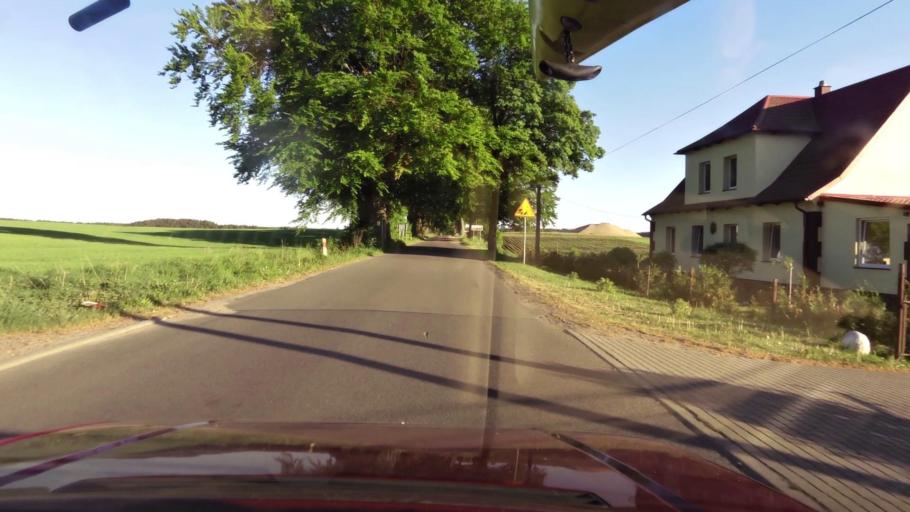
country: PL
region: West Pomeranian Voivodeship
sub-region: Powiat szczecinecki
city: Bialy Bor
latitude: 53.9473
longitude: 16.7855
